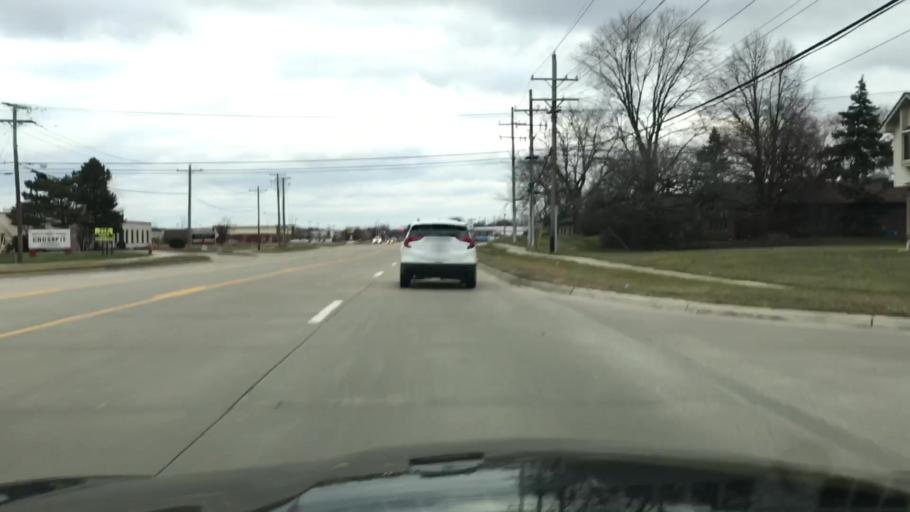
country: US
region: Michigan
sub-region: Oakland County
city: Clawson
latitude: 42.5569
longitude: -83.1079
